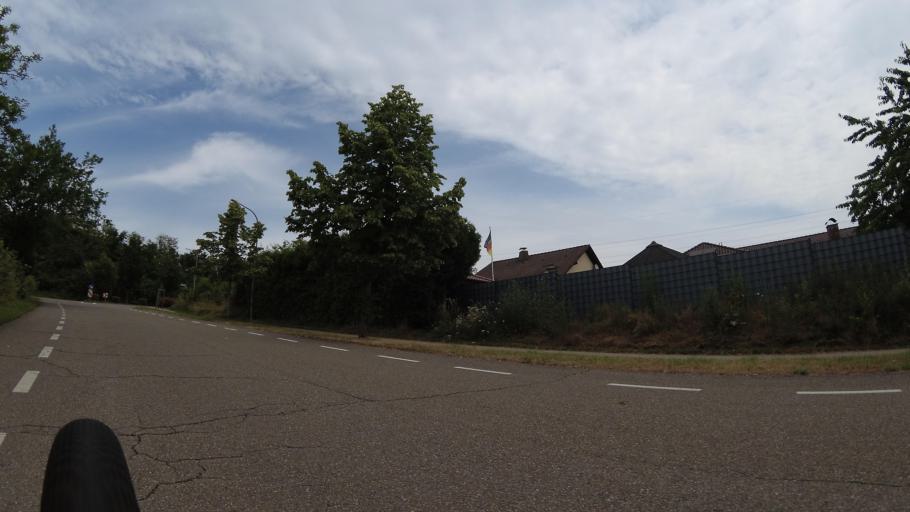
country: DE
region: Saarland
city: Quierschied
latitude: 49.3190
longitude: 7.0376
